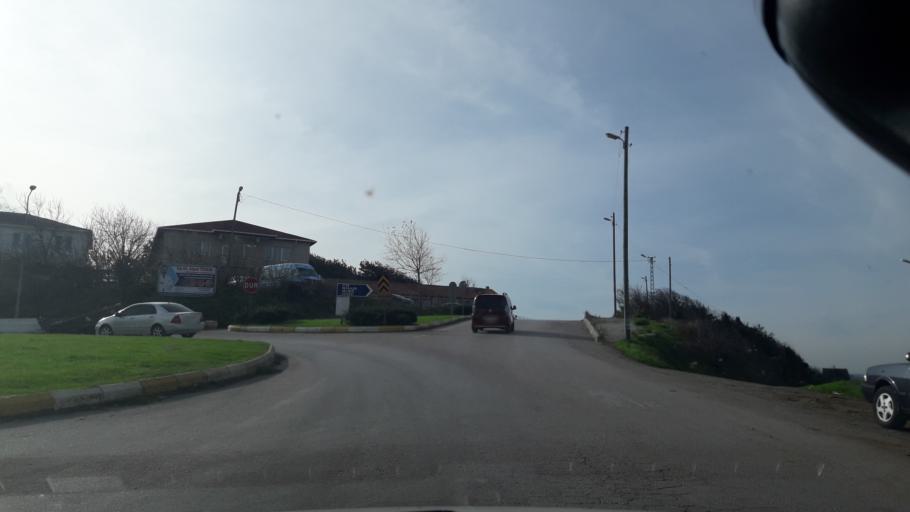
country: TR
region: Sinop
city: Sinop
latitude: 42.0247
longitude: 35.1386
